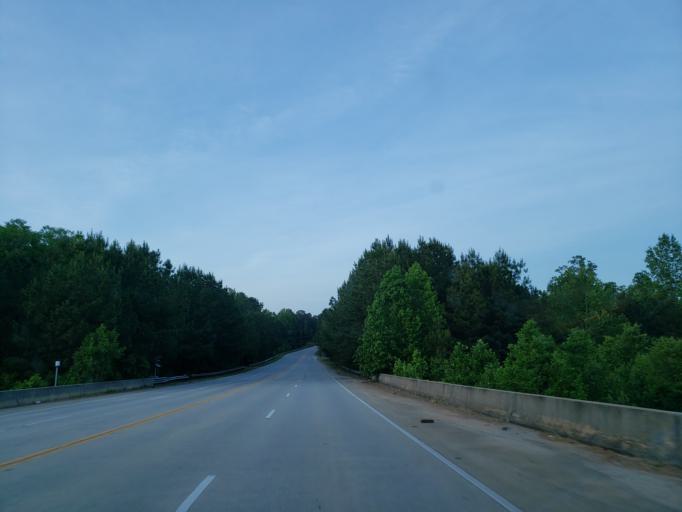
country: US
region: Georgia
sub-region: Fulton County
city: Chattahoochee Hills
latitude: 33.6535
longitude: -84.8212
